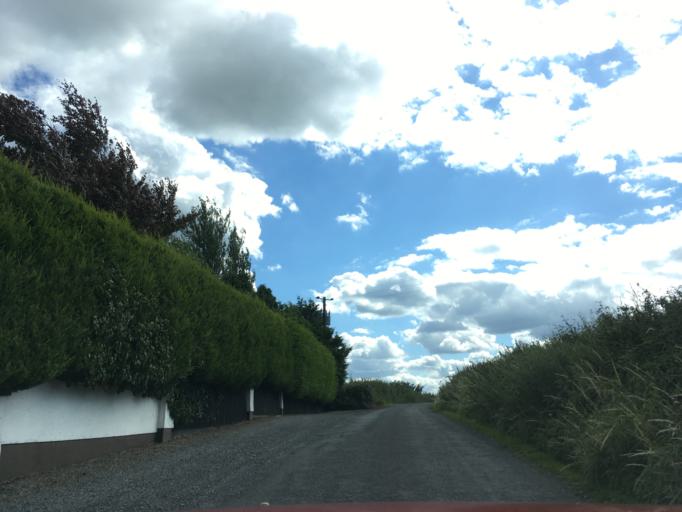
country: IE
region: Munster
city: Cashel
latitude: 52.4961
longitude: -7.9304
